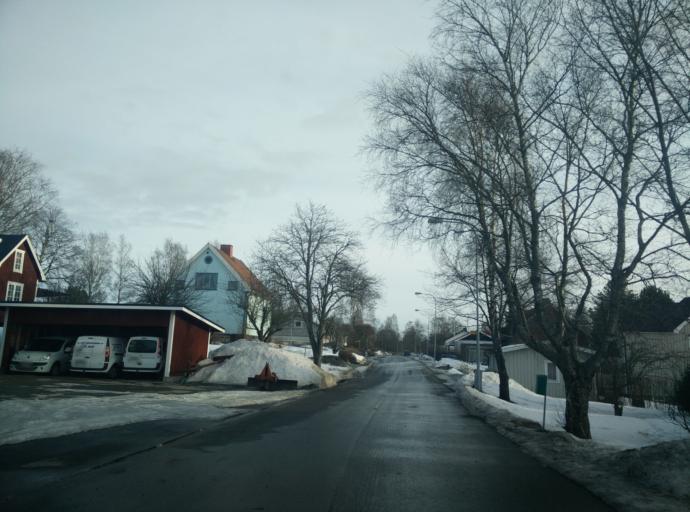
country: SE
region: Vaesternorrland
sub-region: Sundsvalls Kommun
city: Johannedal
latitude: 62.4315
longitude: 17.4186
